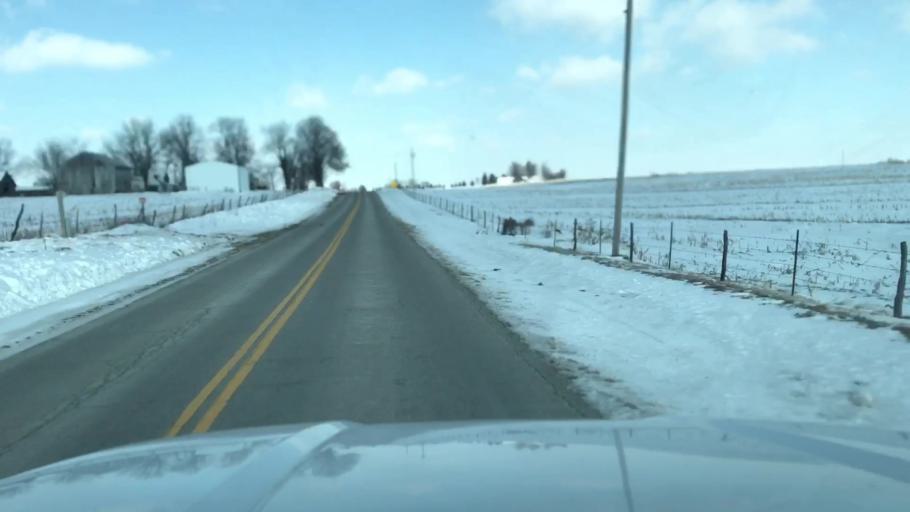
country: US
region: Missouri
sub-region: Nodaway County
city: Maryville
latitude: 40.3553
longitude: -94.7221
